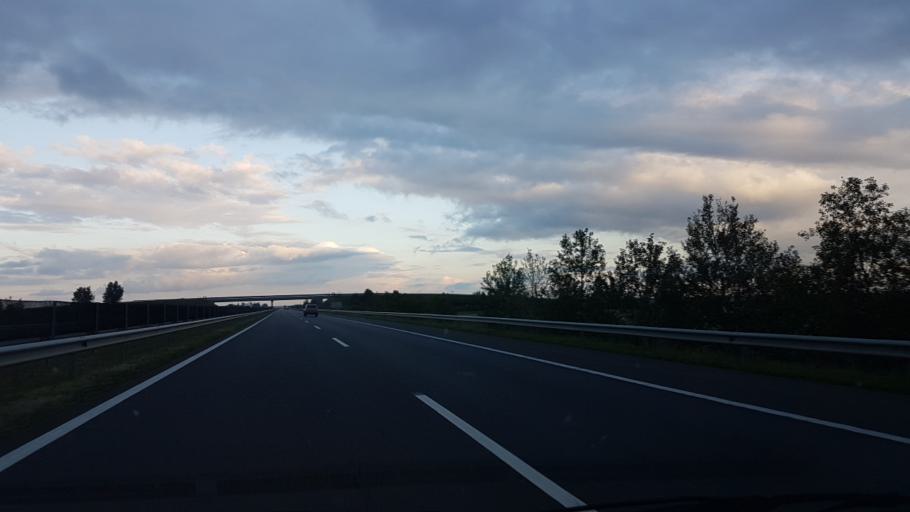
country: HU
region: Borsod-Abauj-Zemplen
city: Malyi
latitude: 48.0295
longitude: 20.8628
